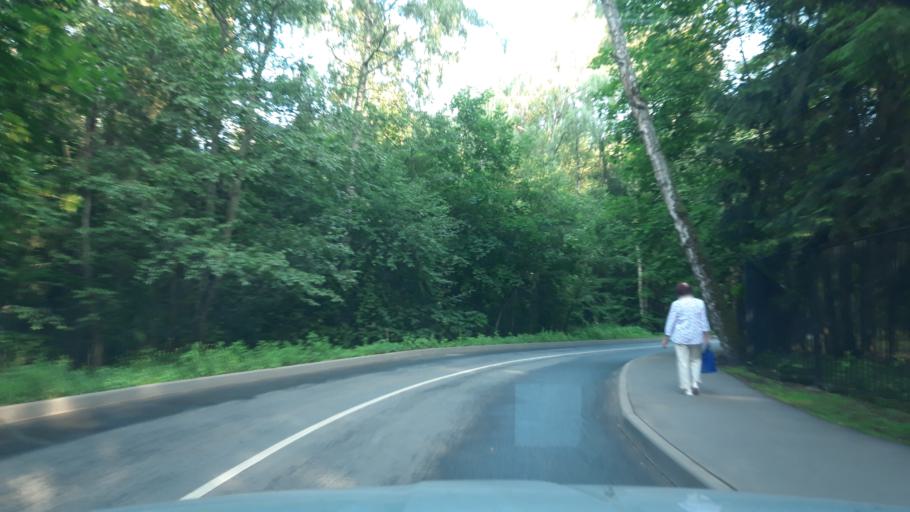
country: RU
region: Moskovskaya
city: Mendeleyevo
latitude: 56.0064
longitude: 37.2133
